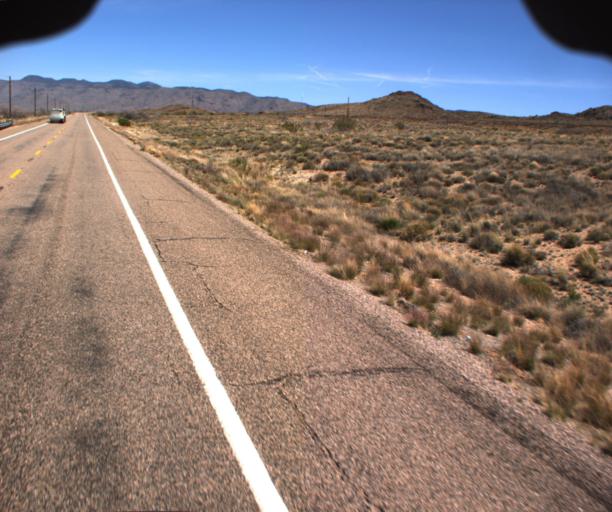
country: US
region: Arizona
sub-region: Mohave County
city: New Kingman-Butler
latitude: 35.4060
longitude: -113.8299
